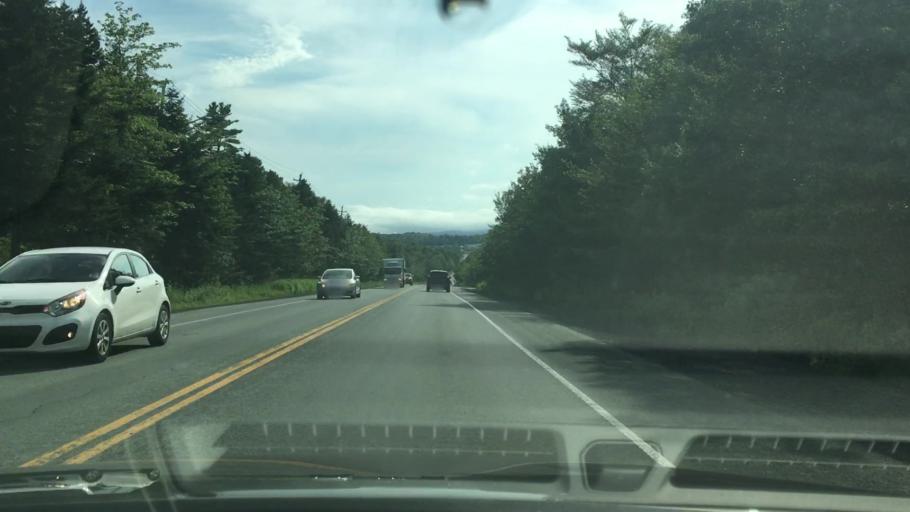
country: CA
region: Nova Scotia
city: Dartmouth
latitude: 44.7120
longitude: -63.8388
